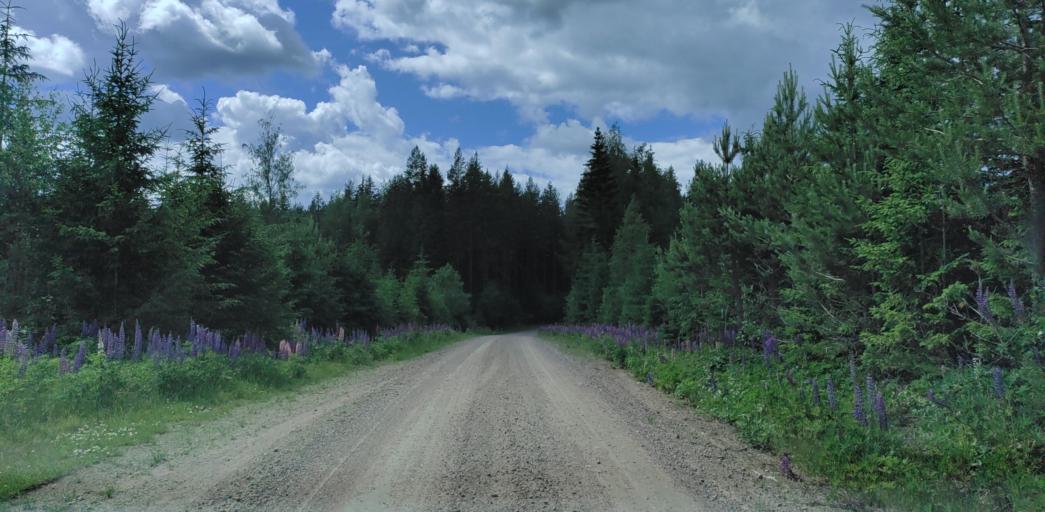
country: SE
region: Vaermland
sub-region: Hagfors Kommun
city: Ekshaerad
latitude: 60.0861
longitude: 13.3236
